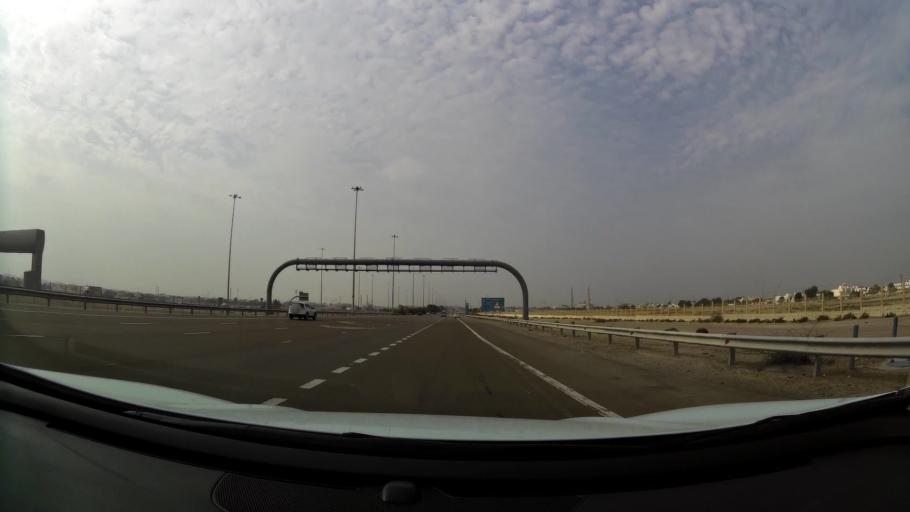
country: AE
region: Abu Dhabi
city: Abu Dhabi
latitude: 24.6777
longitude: 54.7661
